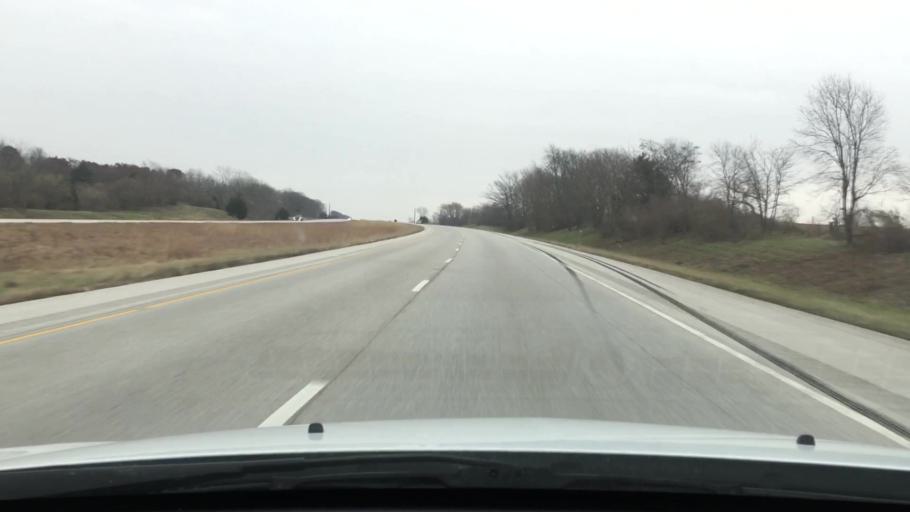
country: US
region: Illinois
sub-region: Scott County
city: Winchester
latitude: 39.6803
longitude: -90.3874
